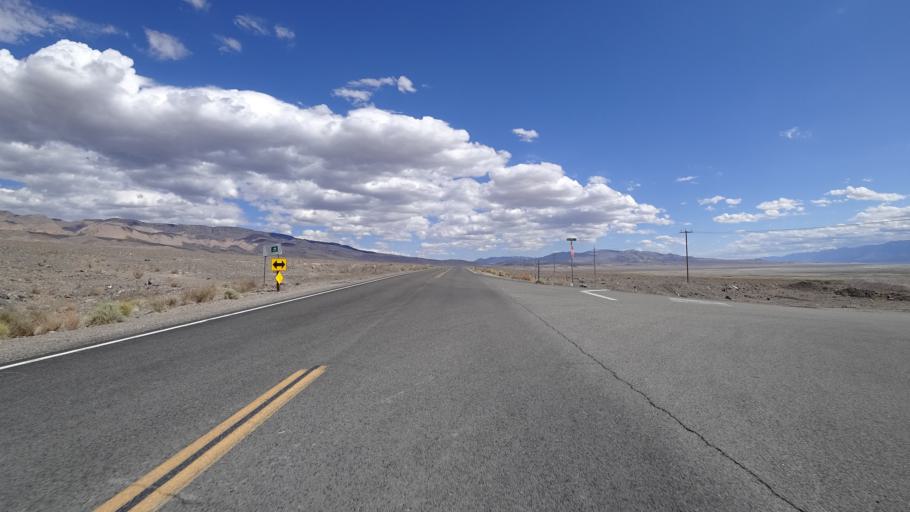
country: US
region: California
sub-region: Inyo County
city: Lone Pine
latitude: 36.4691
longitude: -117.8521
